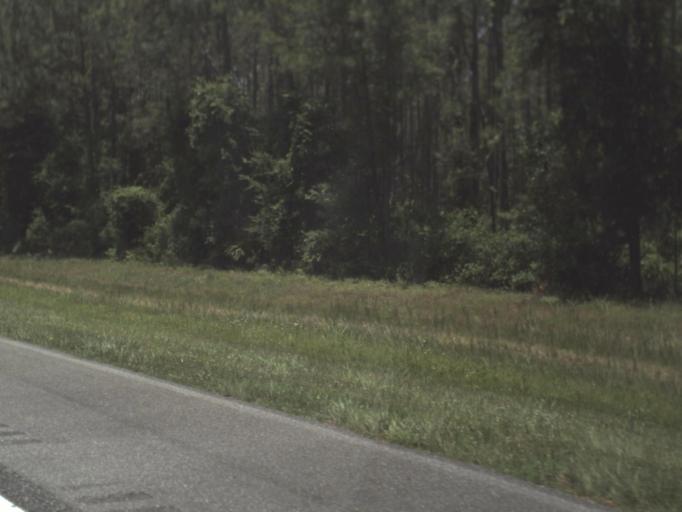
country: US
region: Florida
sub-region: Columbia County
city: Watertown
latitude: 30.2418
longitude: -82.5940
